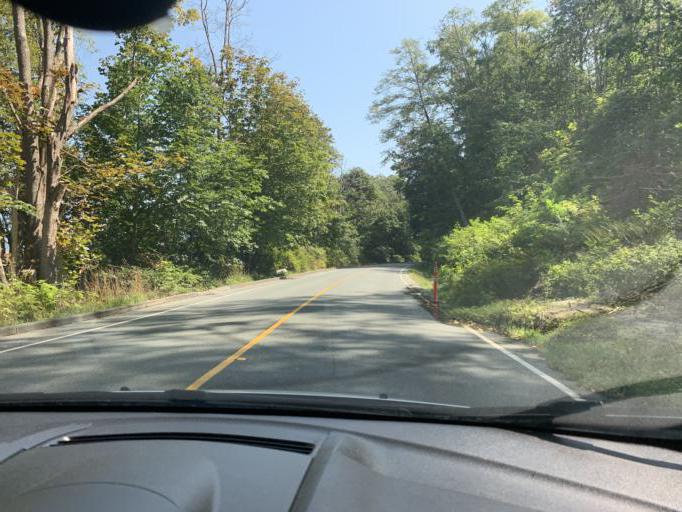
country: CA
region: British Columbia
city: West End
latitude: 49.2792
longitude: -123.2397
